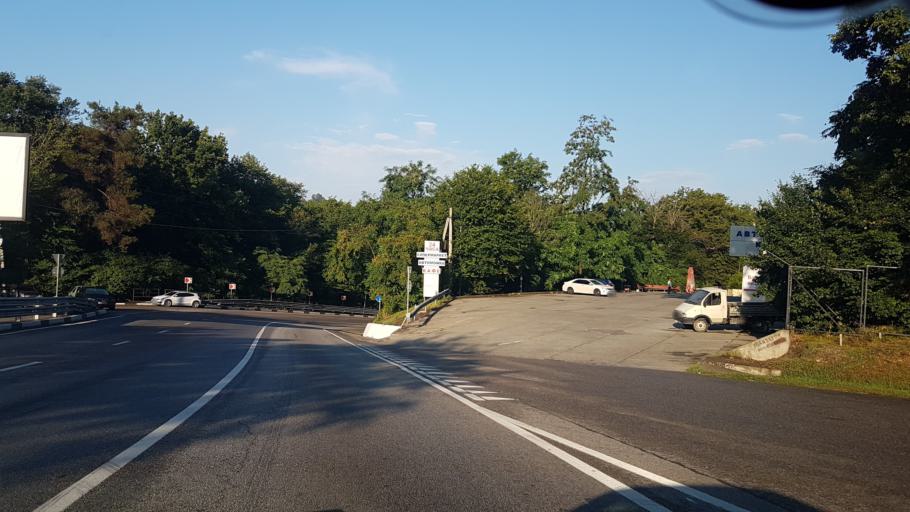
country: RU
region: Krasnodarskiy
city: Dagomys
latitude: 43.6623
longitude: 39.6777
